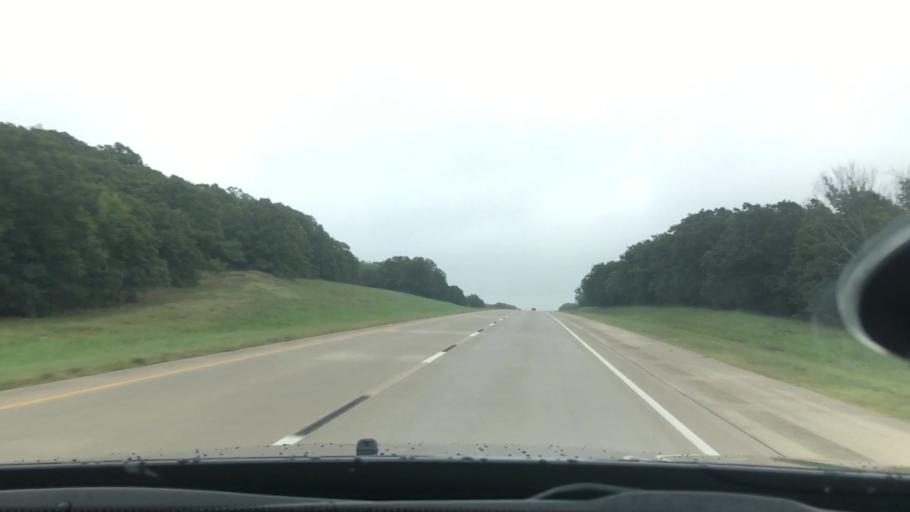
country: US
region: Oklahoma
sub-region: Okfuskee County
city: Boley
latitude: 35.3842
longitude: -96.5743
